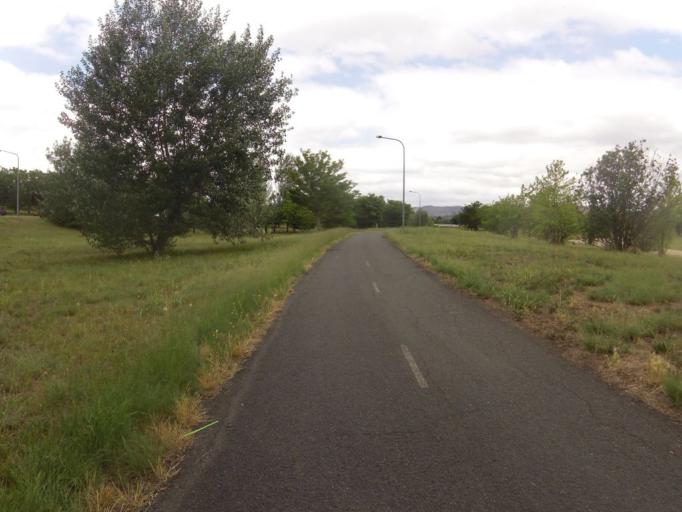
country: AU
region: Australian Capital Territory
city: Macarthur
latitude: -35.4218
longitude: 149.0985
